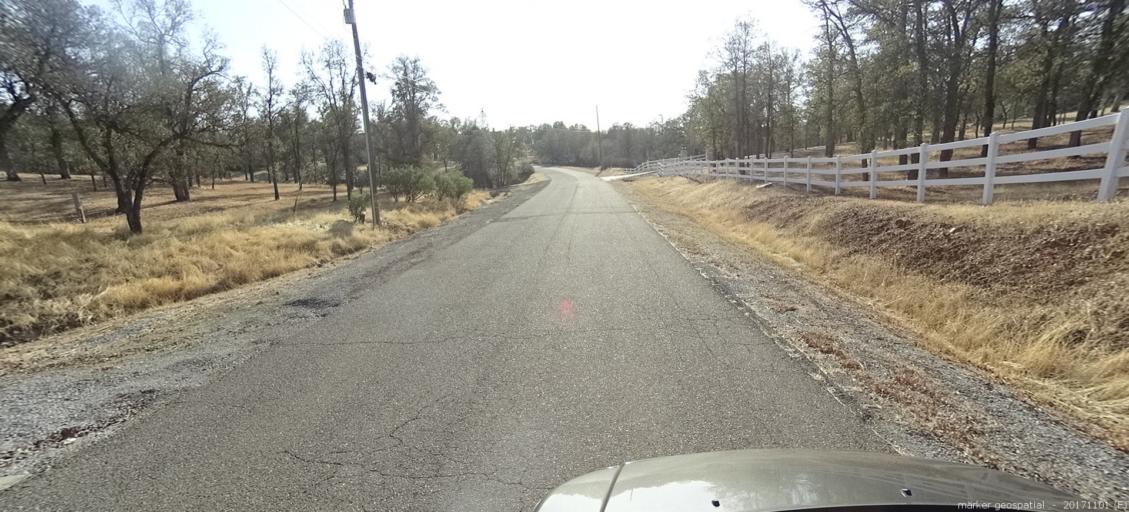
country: US
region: California
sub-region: Shasta County
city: Bella Vista
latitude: 40.6731
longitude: -122.2956
